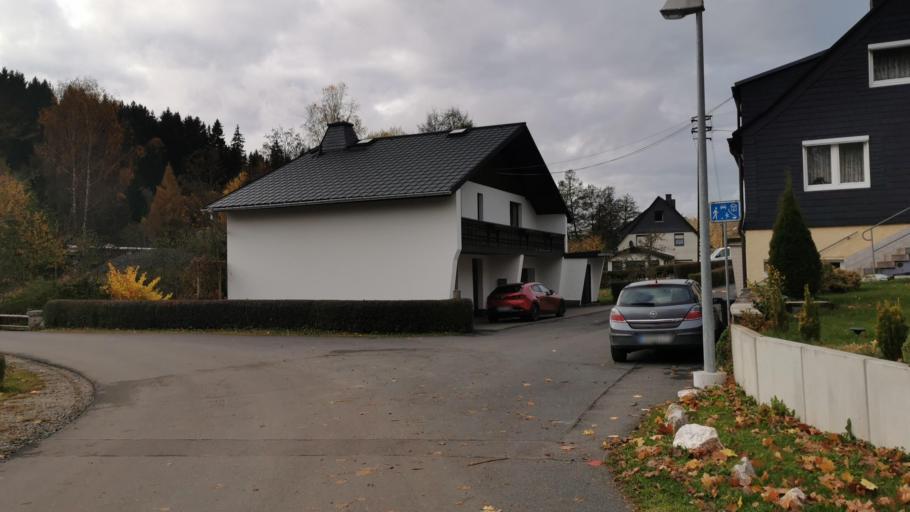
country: DE
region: Thuringia
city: Wurzbach
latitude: 50.4524
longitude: 11.5388
